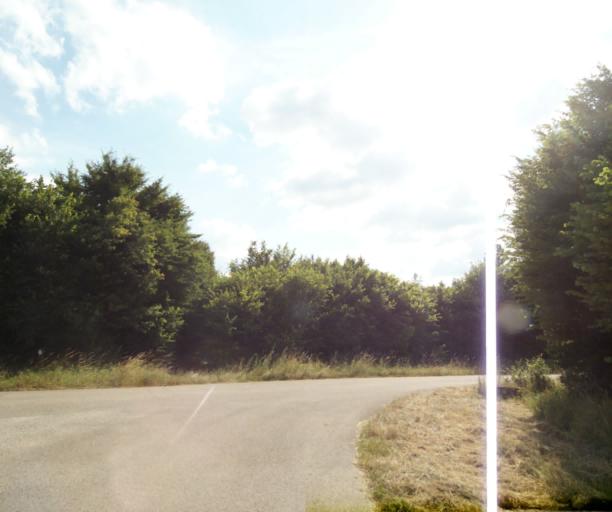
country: FR
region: Lorraine
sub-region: Departement de Meurthe-et-Moselle
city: Chanteheux
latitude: 48.5731
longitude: 6.5507
